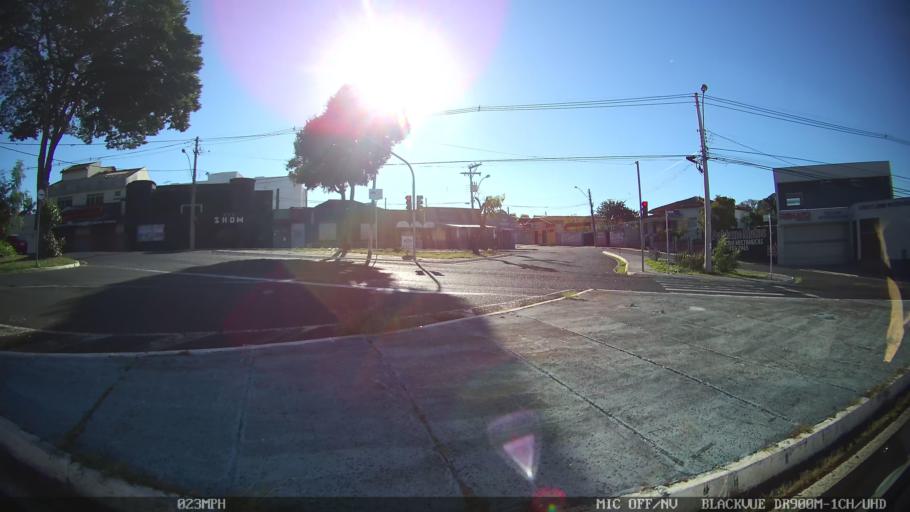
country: BR
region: Sao Paulo
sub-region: Franca
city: Franca
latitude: -20.5508
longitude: -47.3967
